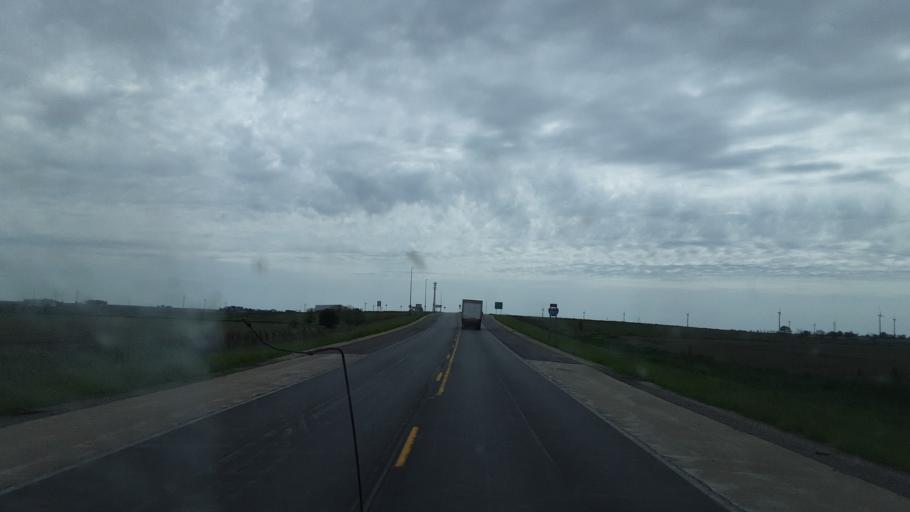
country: US
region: Illinois
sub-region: Tazewell County
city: Richmond
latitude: 40.3080
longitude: -89.4601
